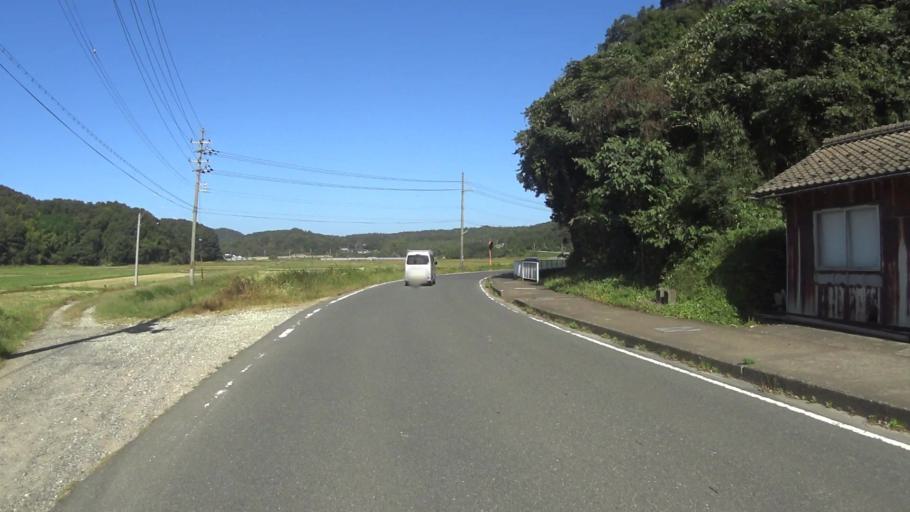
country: JP
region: Kyoto
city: Miyazu
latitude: 35.6863
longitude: 135.0515
